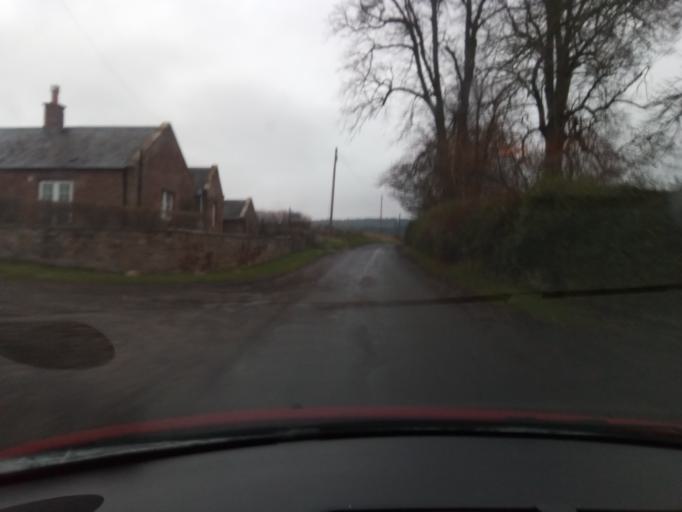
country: GB
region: Scotland
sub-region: The Scottish Borders
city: Kelso
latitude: 55.5387
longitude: -2.4448
